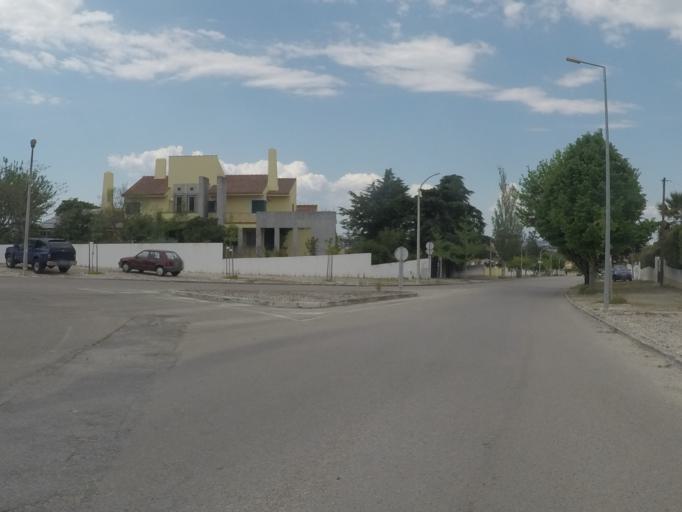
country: PT
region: Setubal
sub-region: Palmela
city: Quinta do Anjo
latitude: 38.5158
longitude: -9.0085
